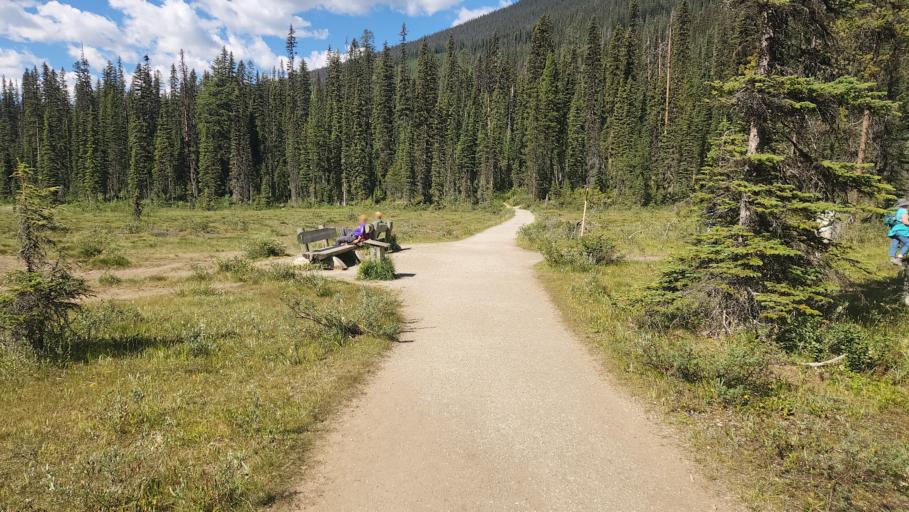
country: CA
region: Alberta
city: Lake Louise
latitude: 51.4508
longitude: -116.5325
